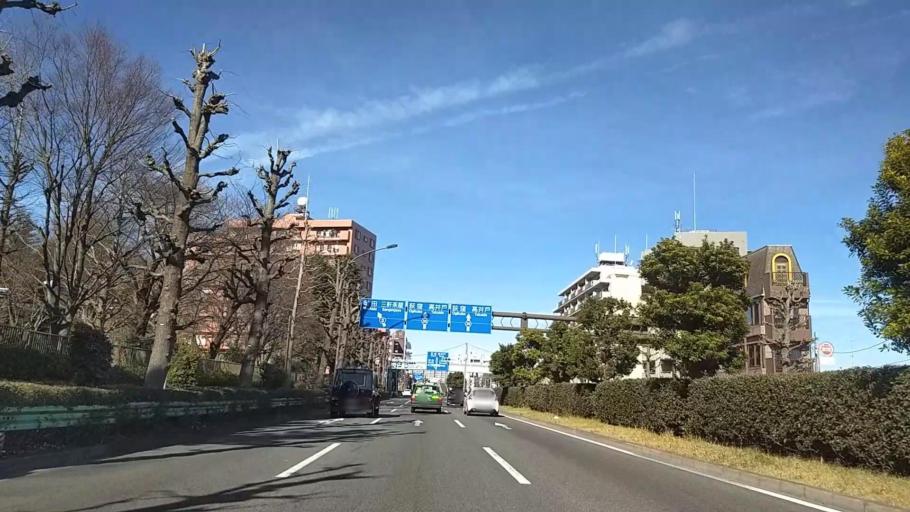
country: JP
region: Tokyo
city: Chofugaoka
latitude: 35.6337
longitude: 139.6235
